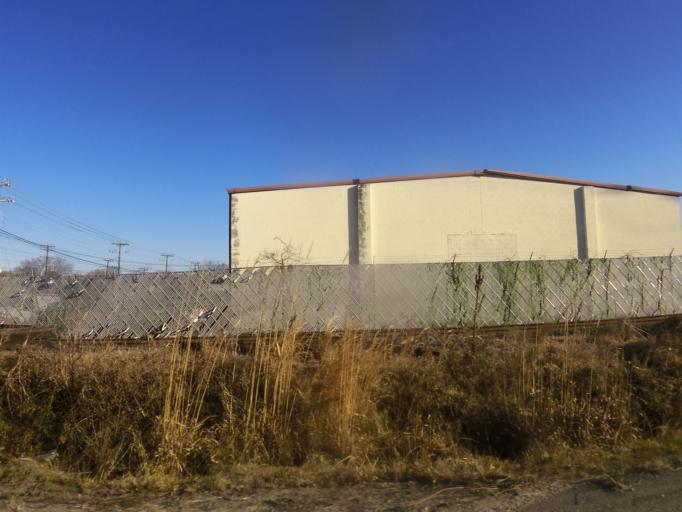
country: US
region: Virginia
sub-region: City of Hopewell
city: Hopewell
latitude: 37.2924
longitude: -77.2802
